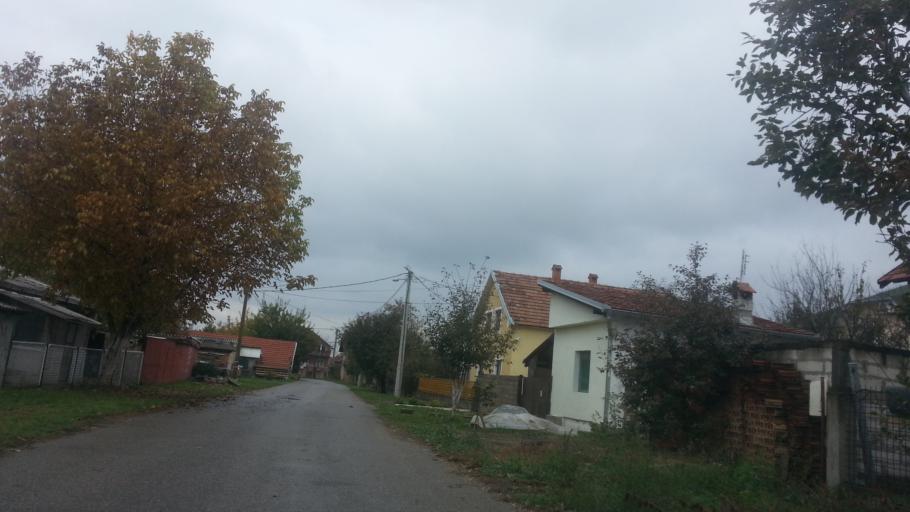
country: RS
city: Novi Banovci
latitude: 44.9078
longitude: 20.2826
